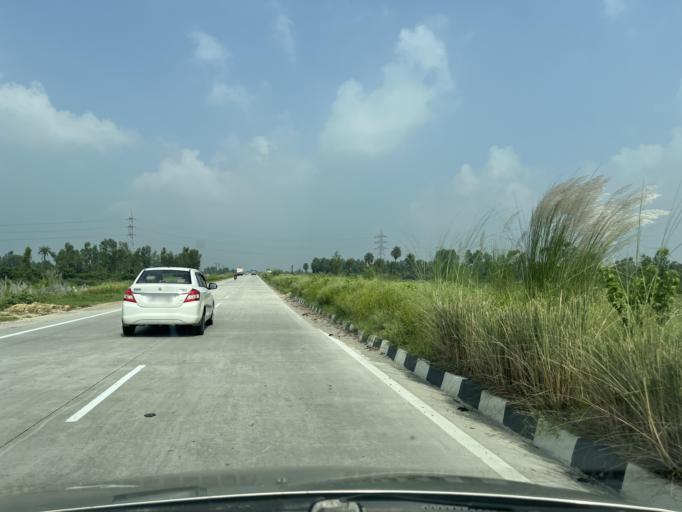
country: IN
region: Uttarakhand
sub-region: Udham Singh Nagar
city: Kashipur
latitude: 29.1649
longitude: 78.9599
